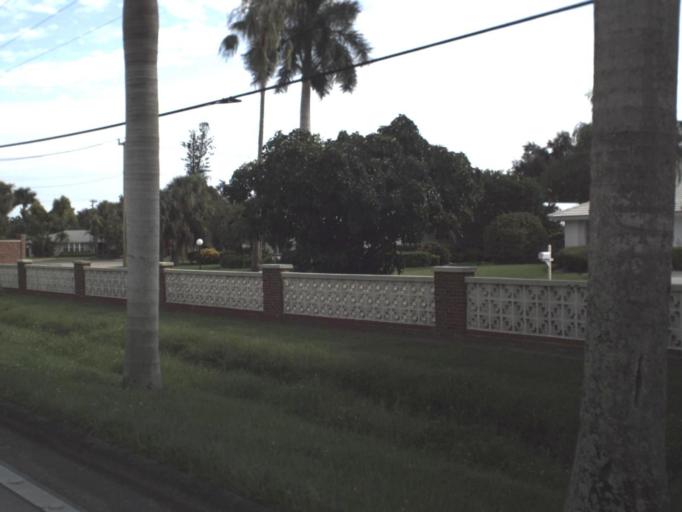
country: US
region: Florida
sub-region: Lee County
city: Whiskey Creek
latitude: 26.5809
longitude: -81.8964
